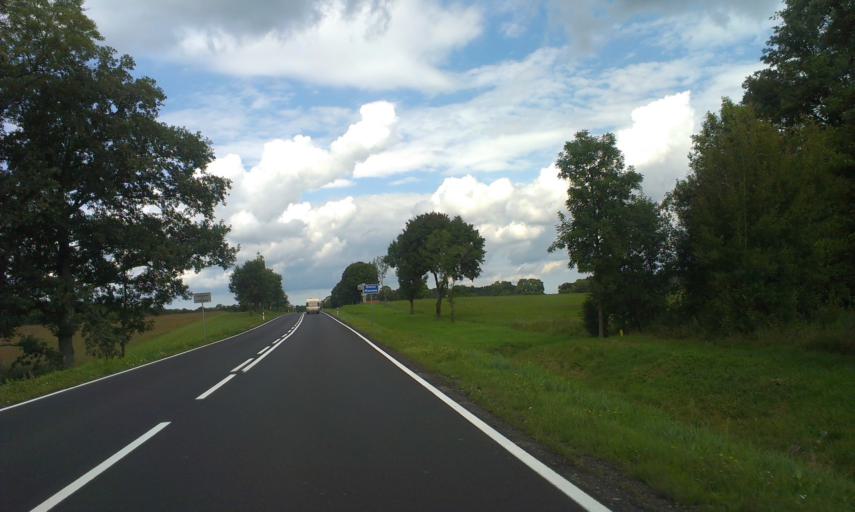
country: PL
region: West Pomeranian Voivodeship
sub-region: Powiat koszalinski
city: Bobolice
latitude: 54.0393
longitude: 16.4564
